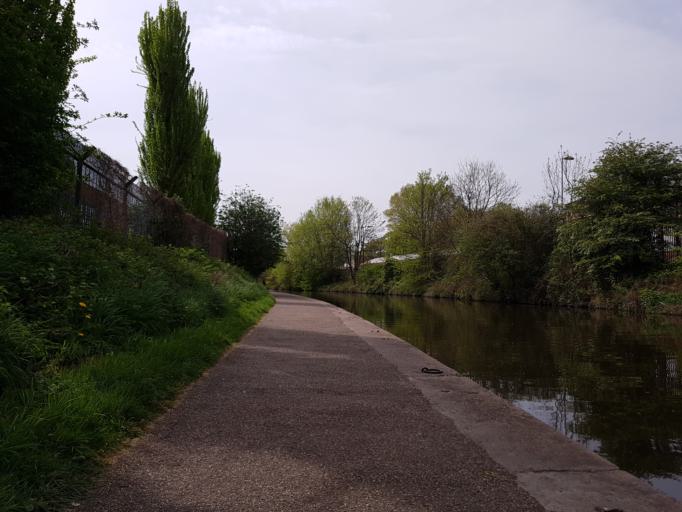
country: GB
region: England
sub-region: Nottingham
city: Nottingham
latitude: 52.9449
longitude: -1.1735
